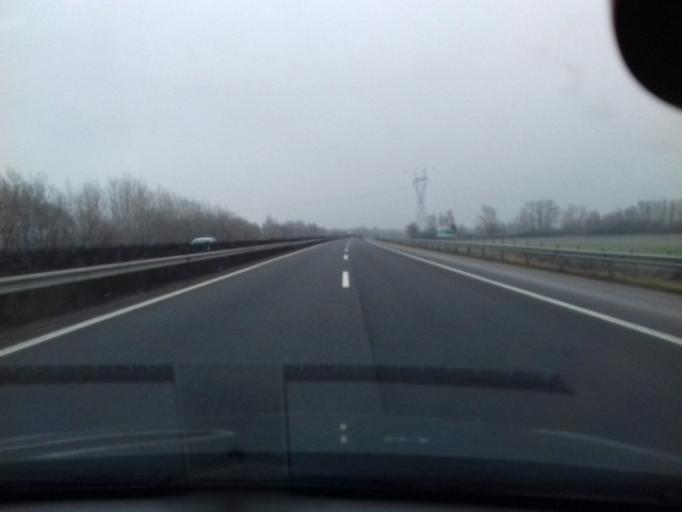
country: HU
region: Borsod-Abauj-Zemplen
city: Hejobaba
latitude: 47.8737
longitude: 20.9484
